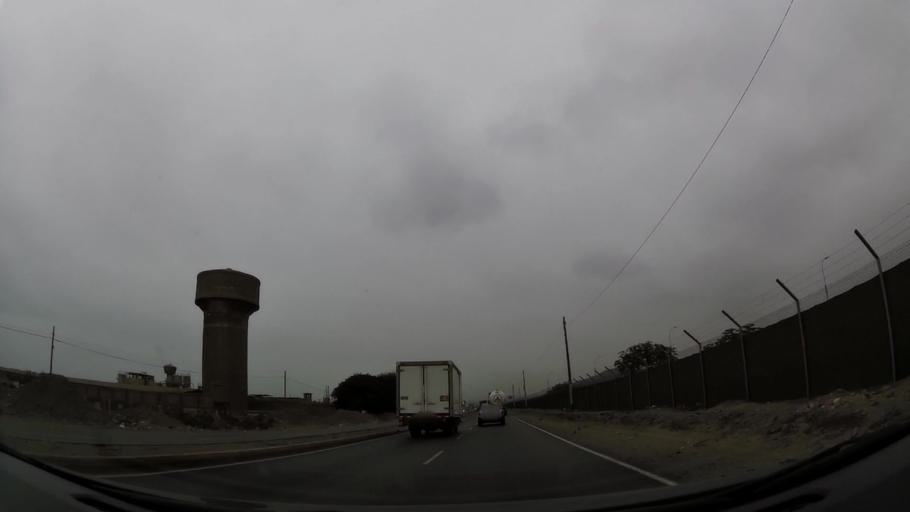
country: PE
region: Callao
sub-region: Callao
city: Callao
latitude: -12.0061
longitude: -77.1274
